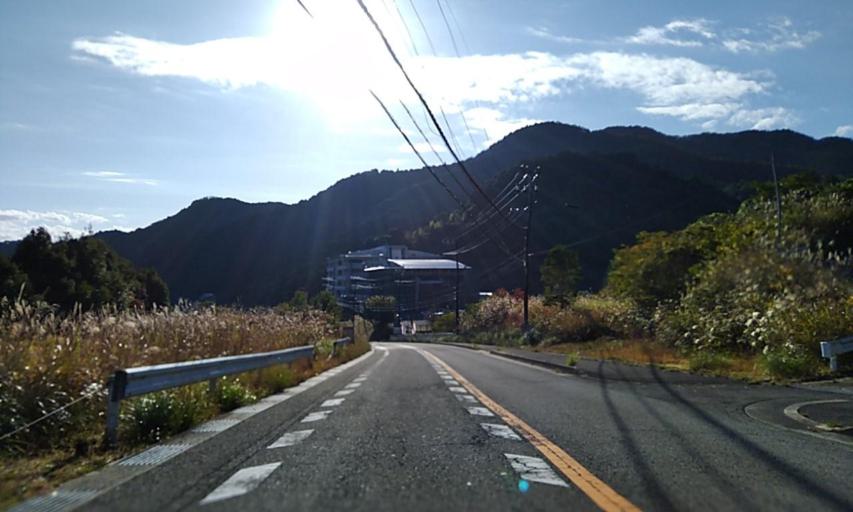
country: JP
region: Wakayama
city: Iwade
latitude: 34.1533
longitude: 135.3090
